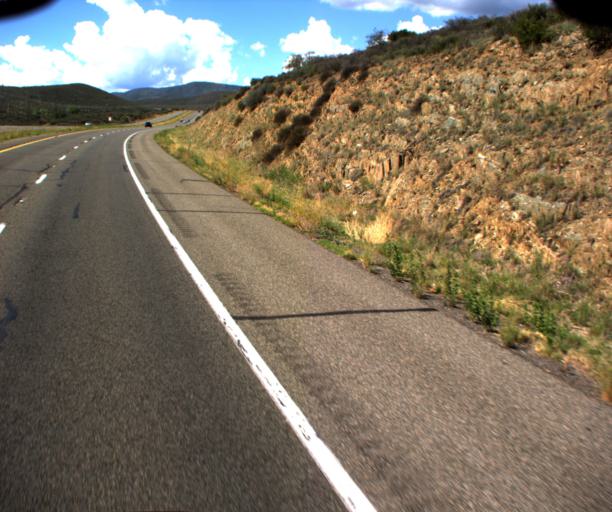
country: US
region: Arizona
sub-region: Yavapai County
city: Dewey-Humboldt
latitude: 34.4716
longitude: -112.2637
